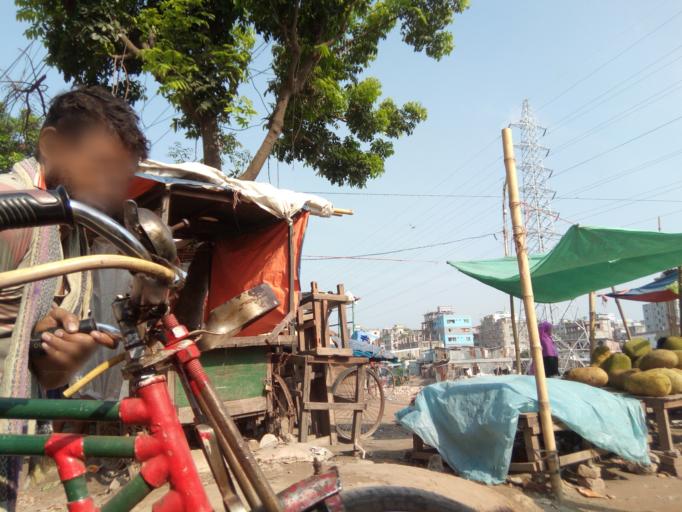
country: BD
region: Dhaka
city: Azimpur
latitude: 23.7145
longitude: 90.3814
